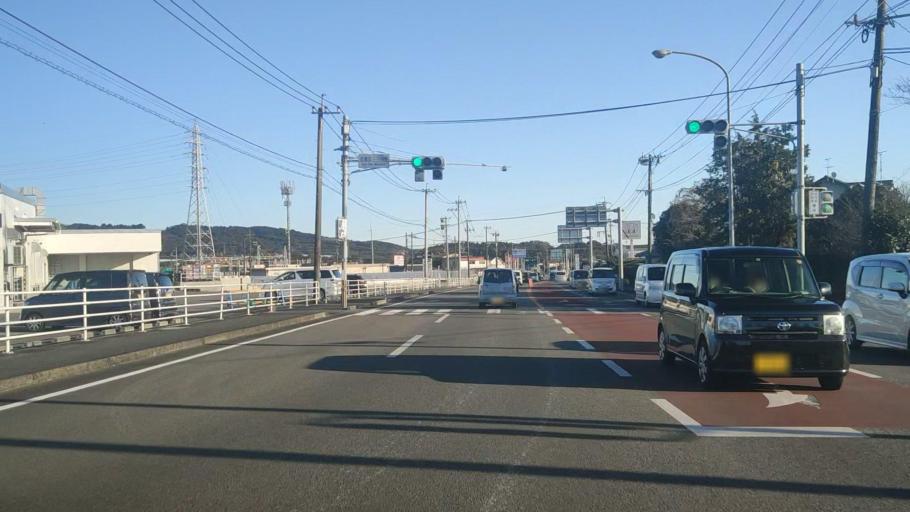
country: JP
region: Miyazaki
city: Takanabe
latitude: 32.2545
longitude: 131.5539
